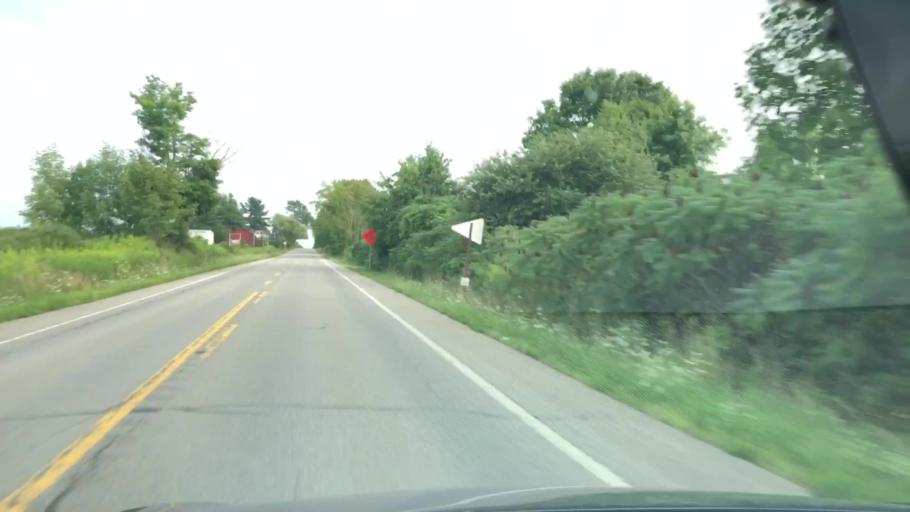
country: US
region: Pennsylvania
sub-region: Erie County
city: Union City
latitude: 41.8130
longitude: -79.8024
